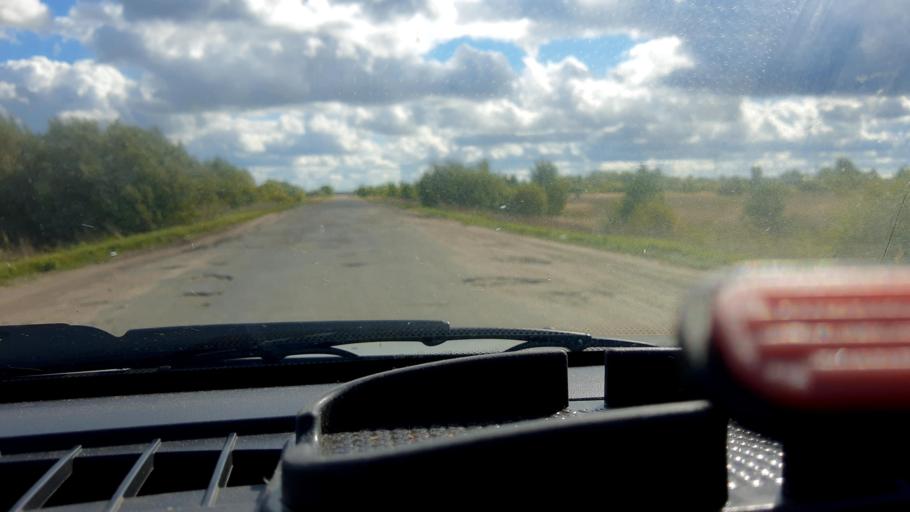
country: RU
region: Nizjnij Novgorod
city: Sharanga
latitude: 56.9413
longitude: 46.6456
